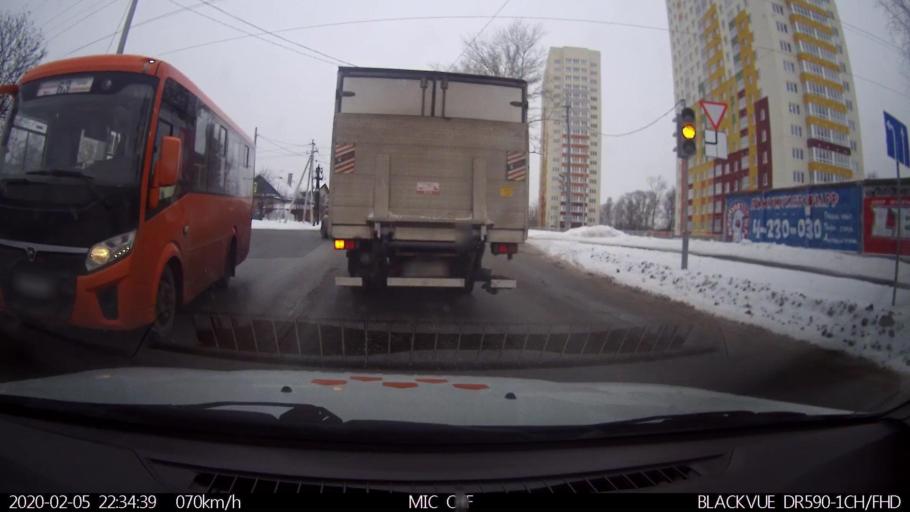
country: RU
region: Nizjnij Novgorod
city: Imeni Stepana Razina
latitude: 54.7357
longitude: 44.2277
